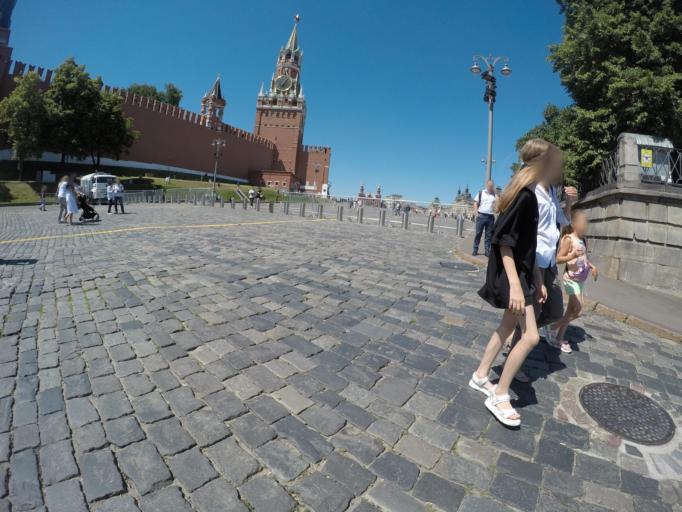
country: RU
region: Moscow
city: Moscow
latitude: 55.7522
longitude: 37.6224
